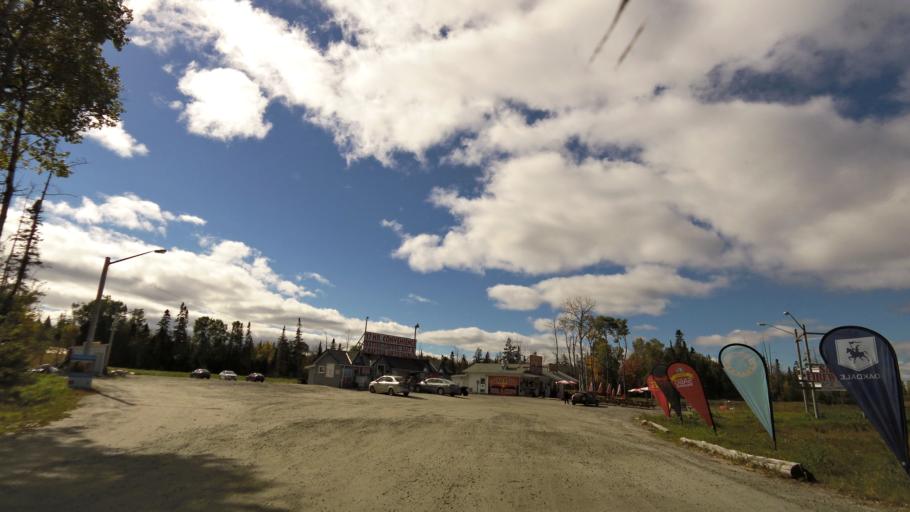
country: CA
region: Ontario
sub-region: Nipissing District
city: North Bay
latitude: 46.3682
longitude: -79.7577
